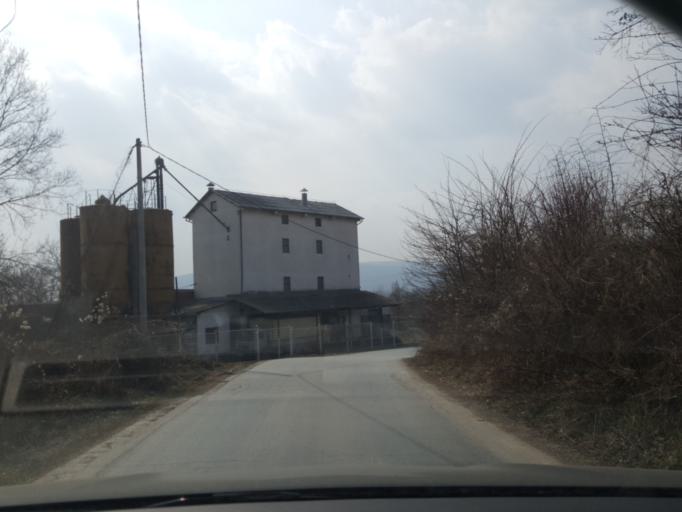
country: RS
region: Central Serbia
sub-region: Nisavski Okrug
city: Nis
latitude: 43.4250
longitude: 21.7982
